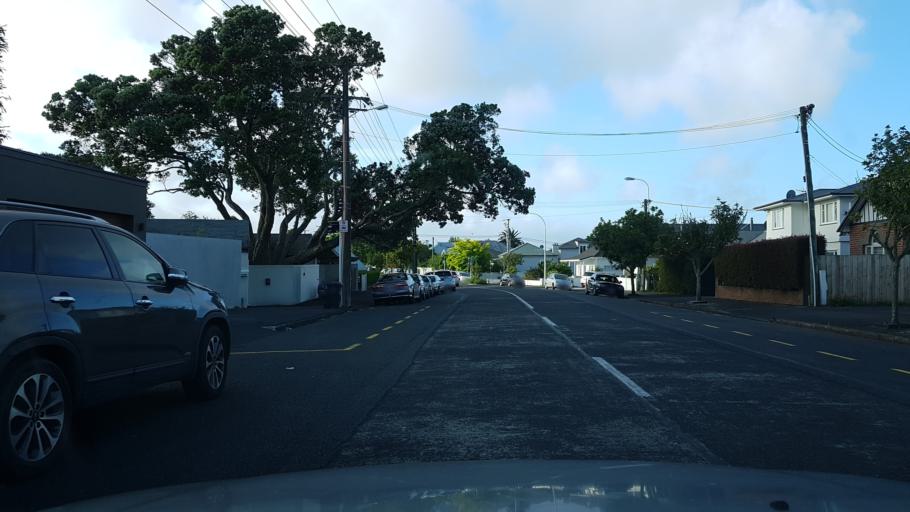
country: NZ
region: Auckland
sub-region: Auckland
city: North Shore
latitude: -36.8207
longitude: 174.7474
